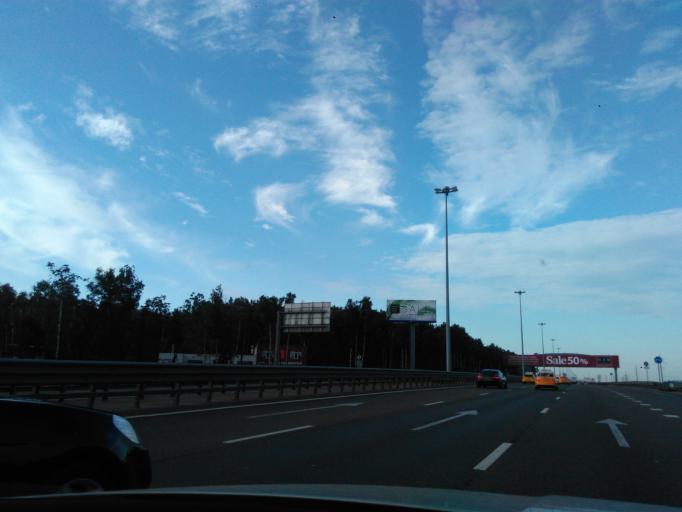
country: RU
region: Moscow
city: Khimki
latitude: 55.9467
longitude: 37.4108
